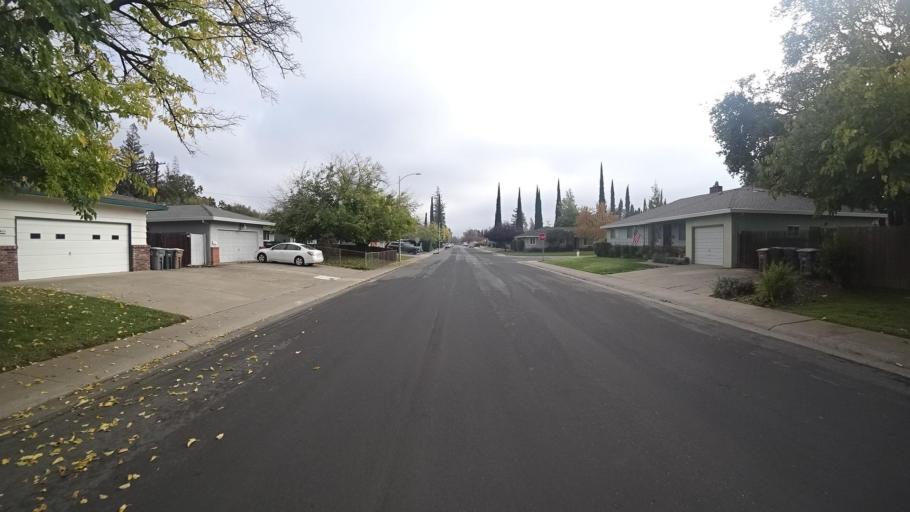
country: US
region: California
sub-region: Sacramento County
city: Elk Grove
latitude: 38.4149
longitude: -121.3674
